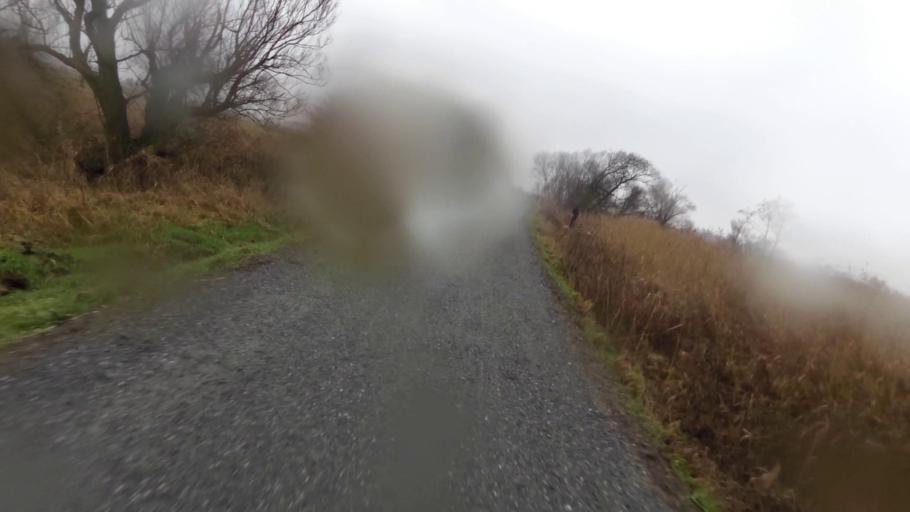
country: PL
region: West Pomeranian Voivodeship
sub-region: Powiat policki
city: Police
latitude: 53.4966
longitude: 14.7008
